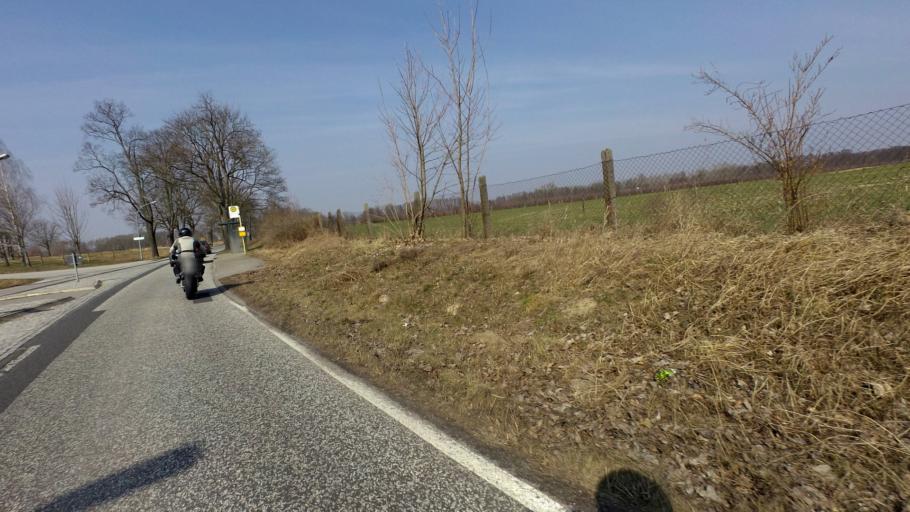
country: DE
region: Brandenburg
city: Ketzin
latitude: 52.4264
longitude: 12.8691
